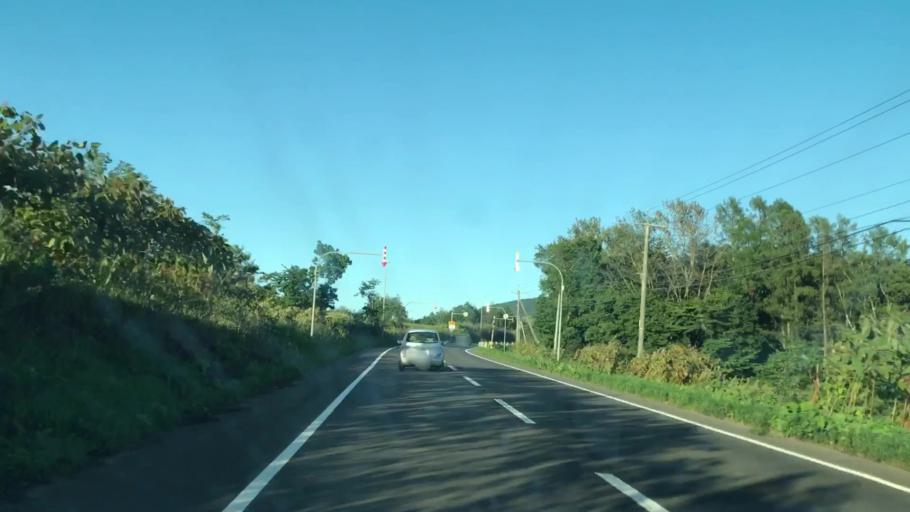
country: JP
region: Hokkaido
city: Niseko Town
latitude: 42.7029
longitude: 140.8508
